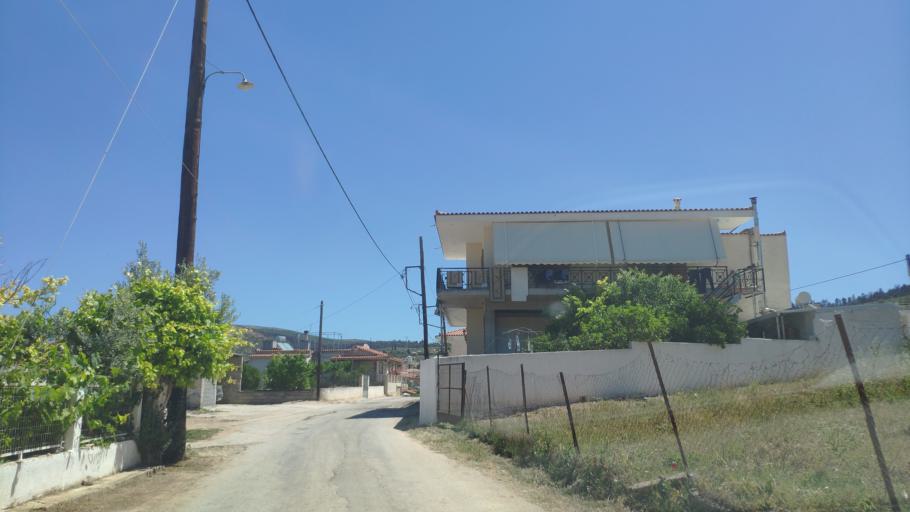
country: GR
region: Peloponnese
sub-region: Nomos Korinthias
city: Athikia
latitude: 37.8138
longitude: 22.9219
